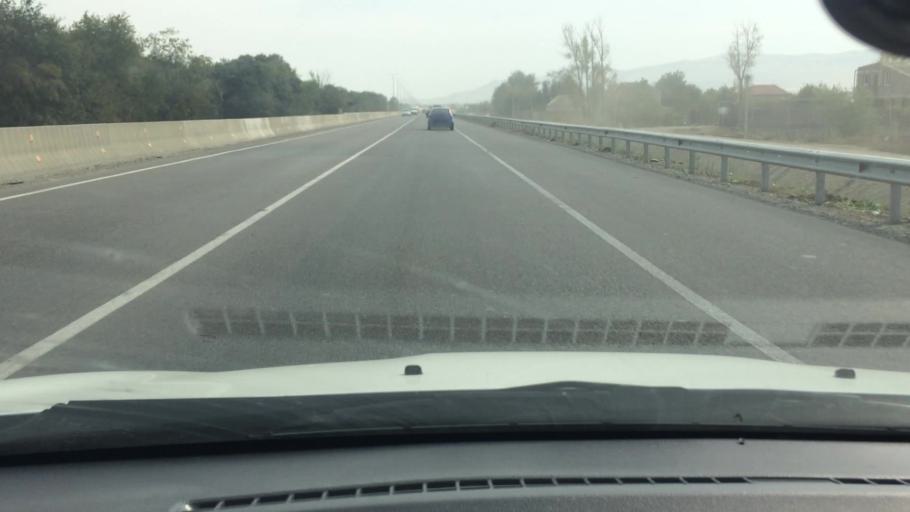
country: GE
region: Kvemo Kartli
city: Rust'avi
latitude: 41.6231
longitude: 44.9257
